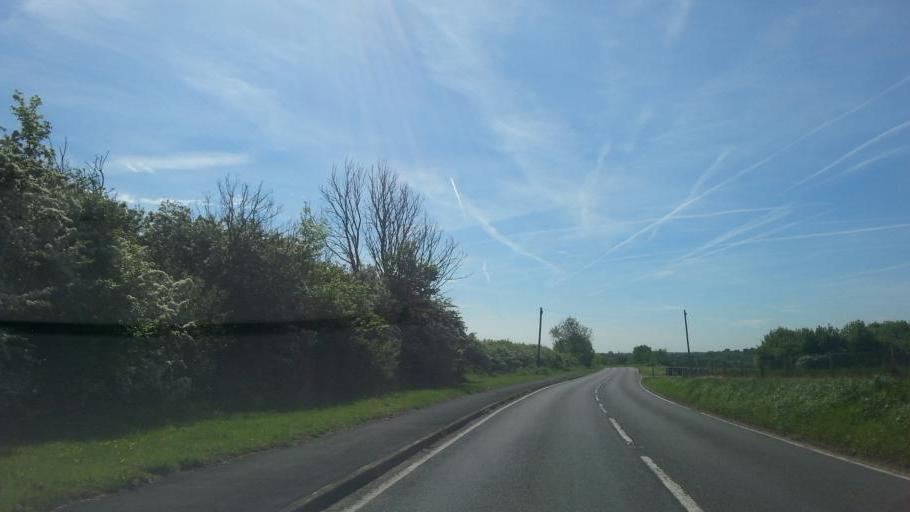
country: GB
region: England
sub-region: Cambridgeshire
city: Great Stukeley
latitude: 52.3510
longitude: -0.2044
